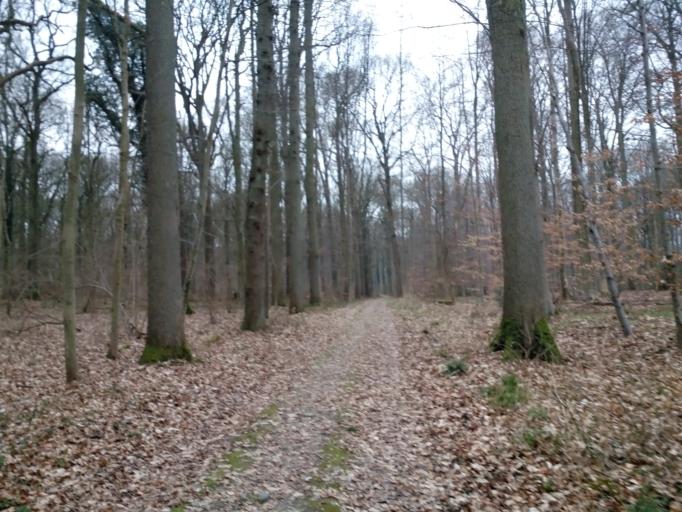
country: BE
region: Flanders
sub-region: Provincie Vlaams-Brabant
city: Oud-Heverlee
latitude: 50.7996
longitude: 4.6746
